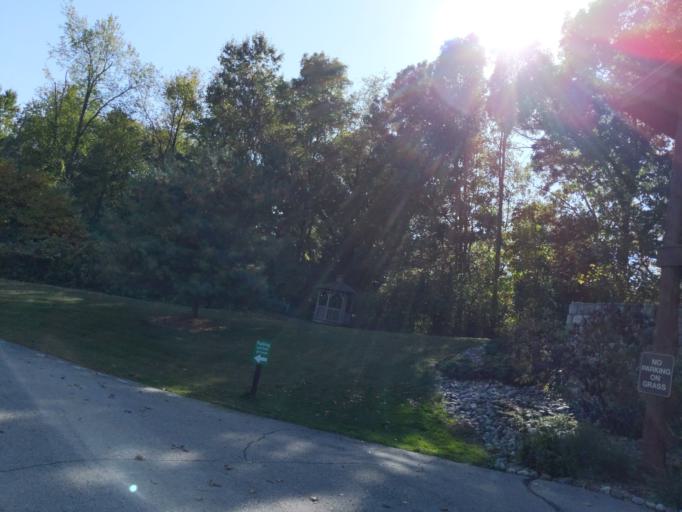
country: US
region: Michigan
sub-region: Clinton County
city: Bath
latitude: 42.8040
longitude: -84.4362
